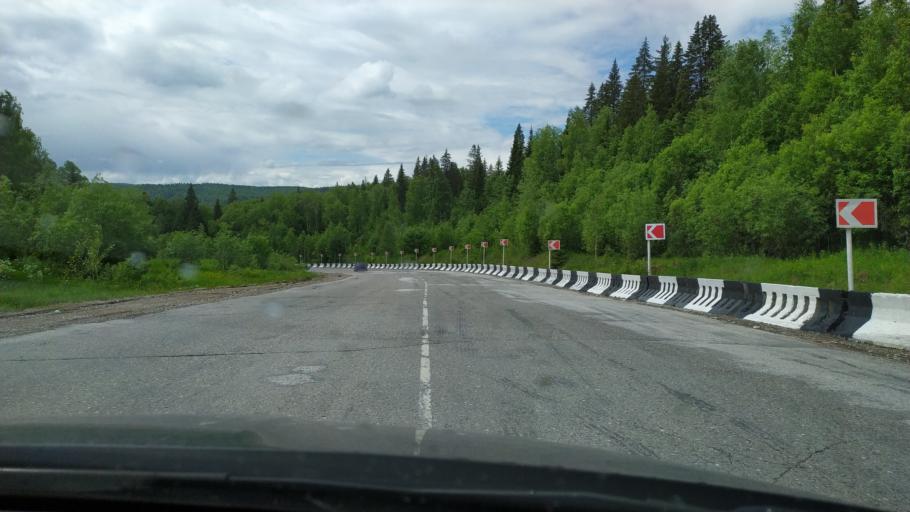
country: RU
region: Perm
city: Gremyachinsk
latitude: 58.4458
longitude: 57.8697
